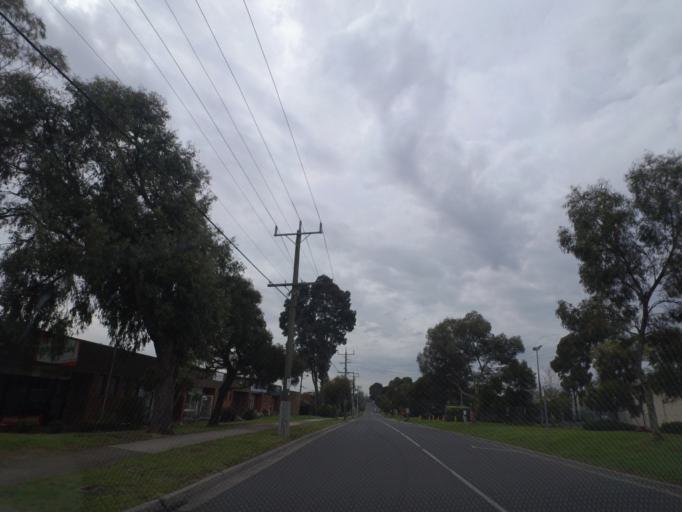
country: AU
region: Victoria
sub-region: Knox
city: Bayswater
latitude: -37.8439
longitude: 145.2790
